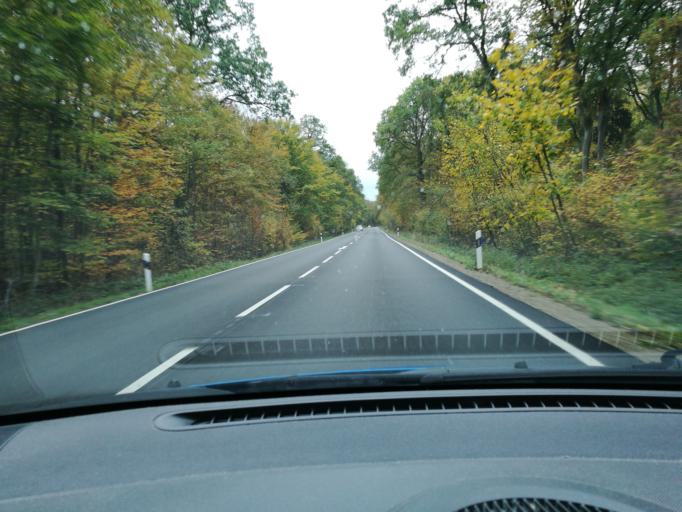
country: DE
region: Schleswig-Holstein
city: Fredeburg
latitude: 53.6628
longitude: 10.7168
